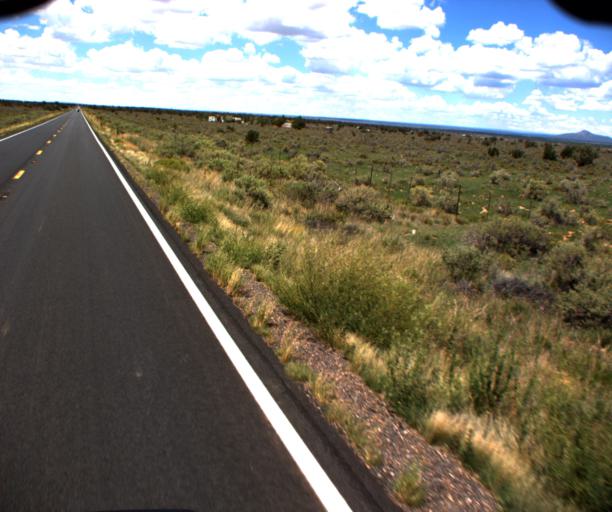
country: US
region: Arizona
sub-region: Coconino County
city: Williams
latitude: 35.6328
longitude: -112.1196
